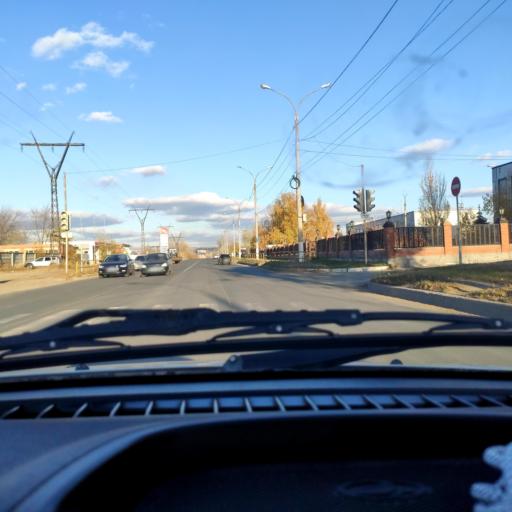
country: RU
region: Samara
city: Zhigulevsk
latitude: 53.4798
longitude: 49.4948
